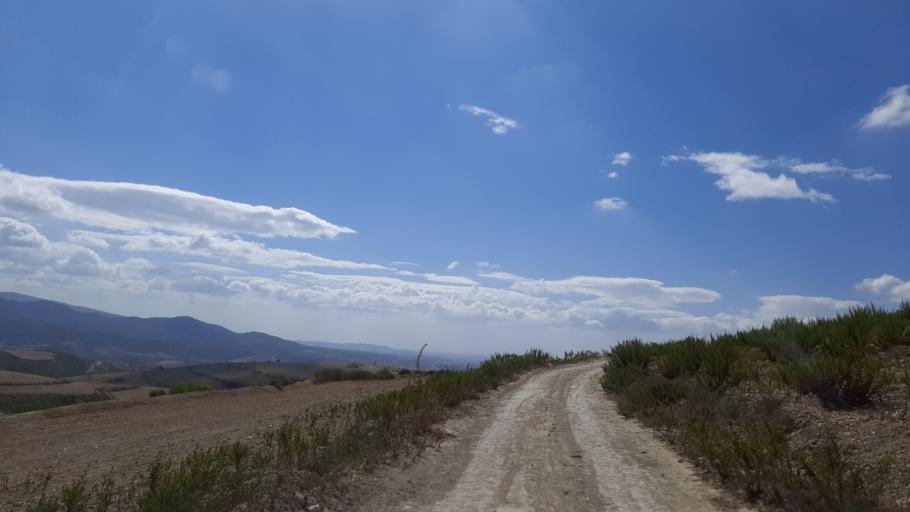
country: TN
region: Zaghwan
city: Zaghouan
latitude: 36.5074
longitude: 10.1842
